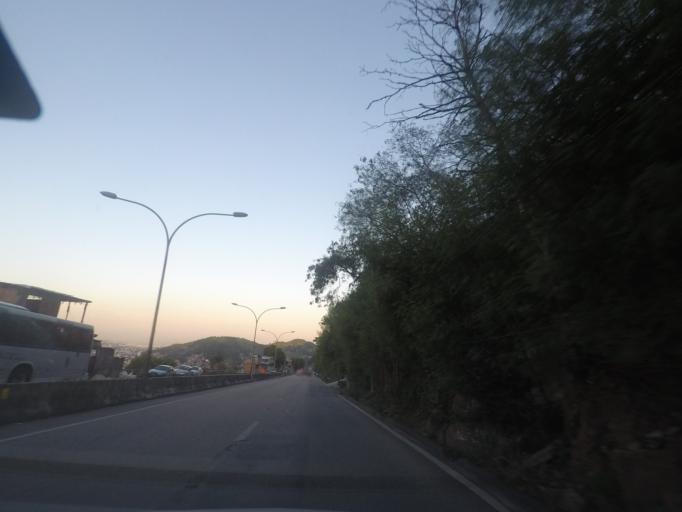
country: BR
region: Rio de Janeiro
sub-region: Rio De Janeiro
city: Rio de Janeiro
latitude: -22.9174
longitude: -43.2793
